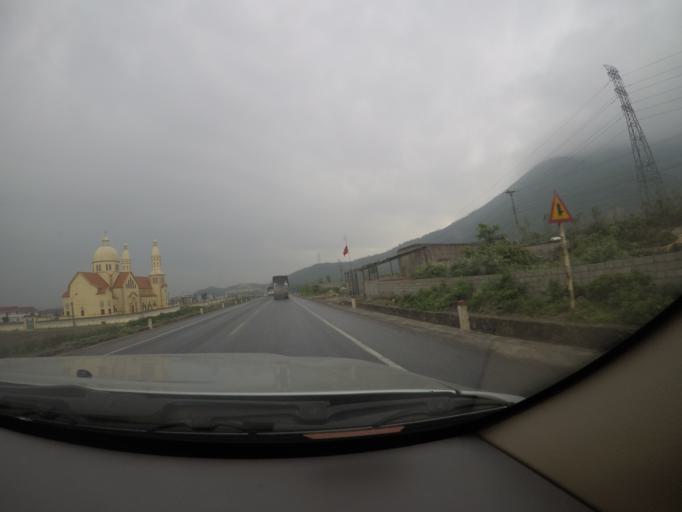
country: VN
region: Ha Tinh
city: Ky Anh
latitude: 17.9969
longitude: 106.4559
